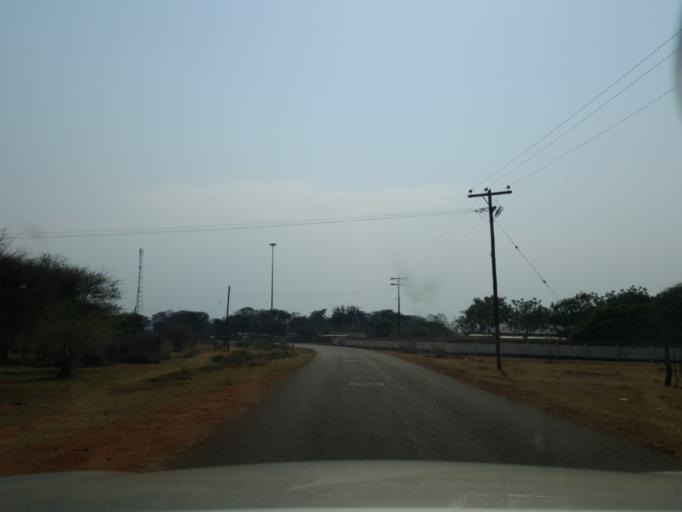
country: BW
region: South East
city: Lobatse
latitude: -25.2869
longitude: 25.9113
